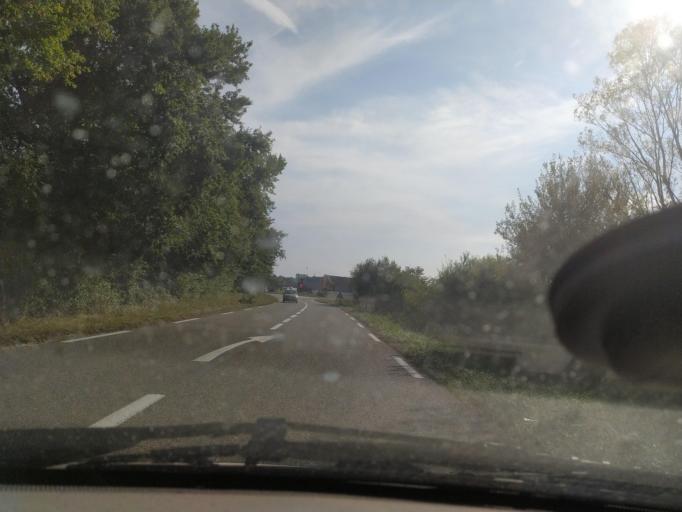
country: FR
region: Midi-Pyrenees
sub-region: Departement du Gers
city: Nogaro
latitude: 43.7712
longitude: -0.0290
